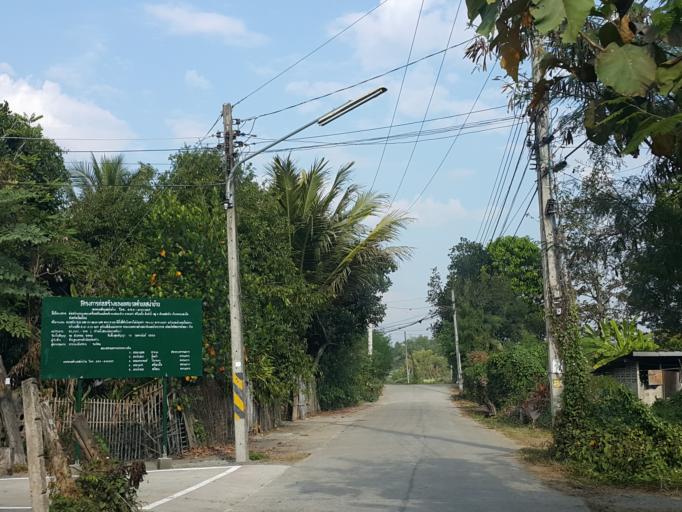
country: TH
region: Chiang Mai
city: San Sai
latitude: 18.8271
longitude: 99.1185
